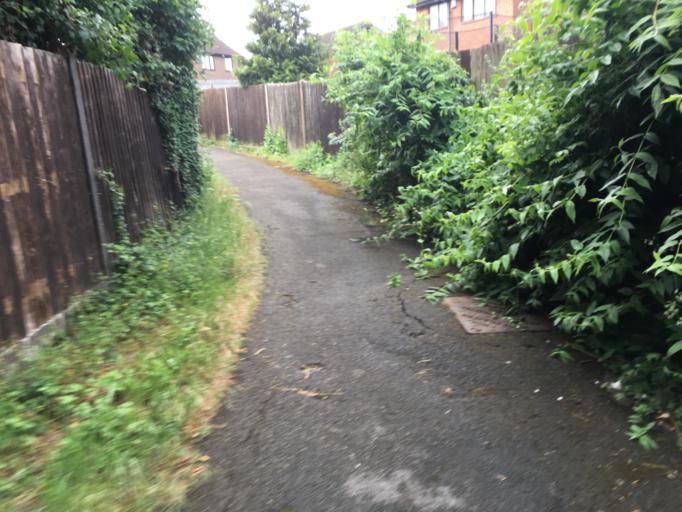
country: GB
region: England
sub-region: West Berkshire
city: Calcot
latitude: 51.4422
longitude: -1.0401
